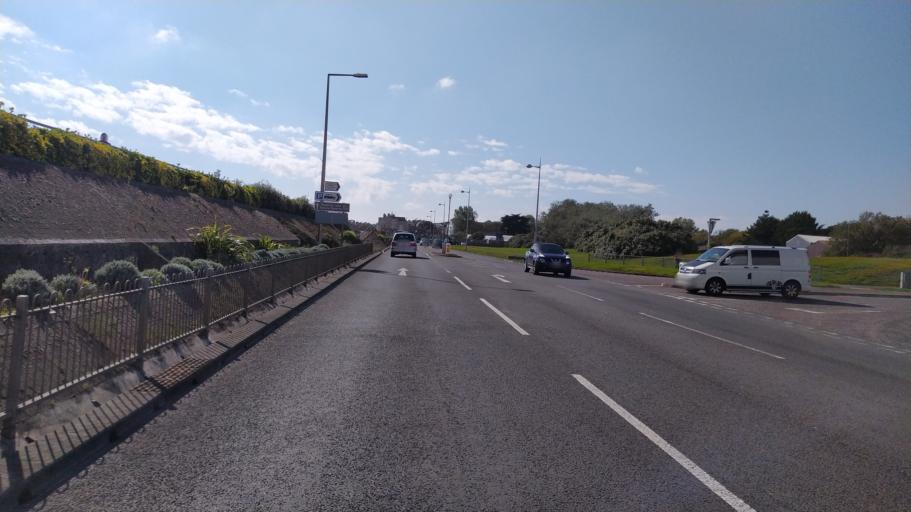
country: GB
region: England
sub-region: Dorset
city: Overcombe
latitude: 50.6270
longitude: -2.4409
